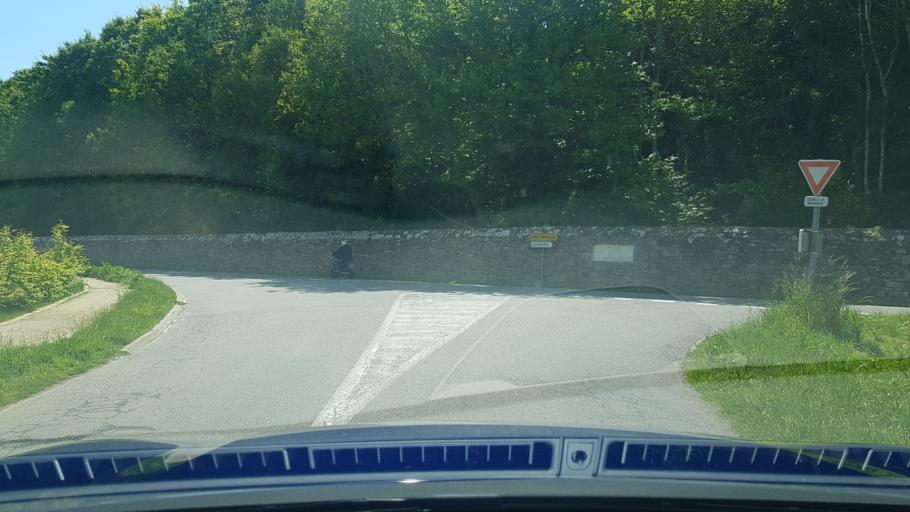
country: FR
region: Brittany
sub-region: Departement du Morbihan
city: Guidel-Plage
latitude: 47.7991
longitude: -3.4974
